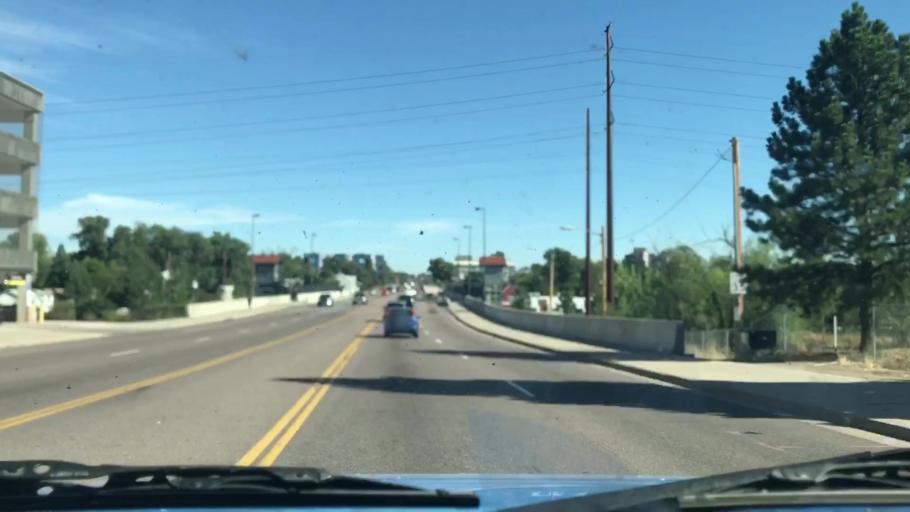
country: US
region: Colorado
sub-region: Jefferson County
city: Edgewater
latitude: 39.7336
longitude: -105.0532
